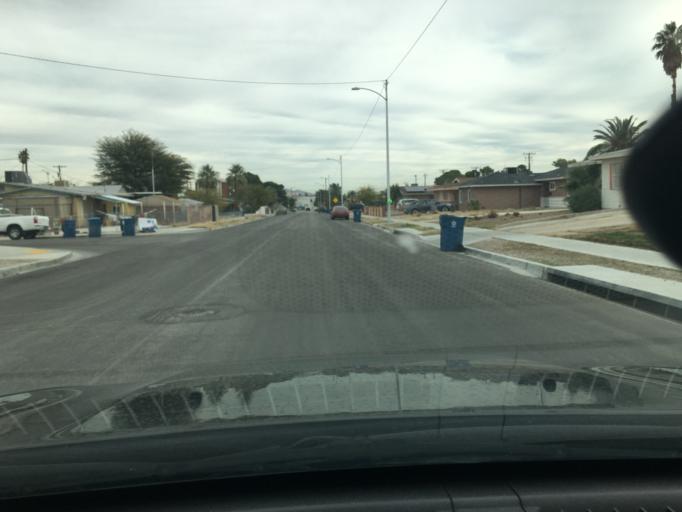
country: US
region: Nevada
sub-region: Clark County
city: Spring Valley
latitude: 36.1632
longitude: -115.2128
